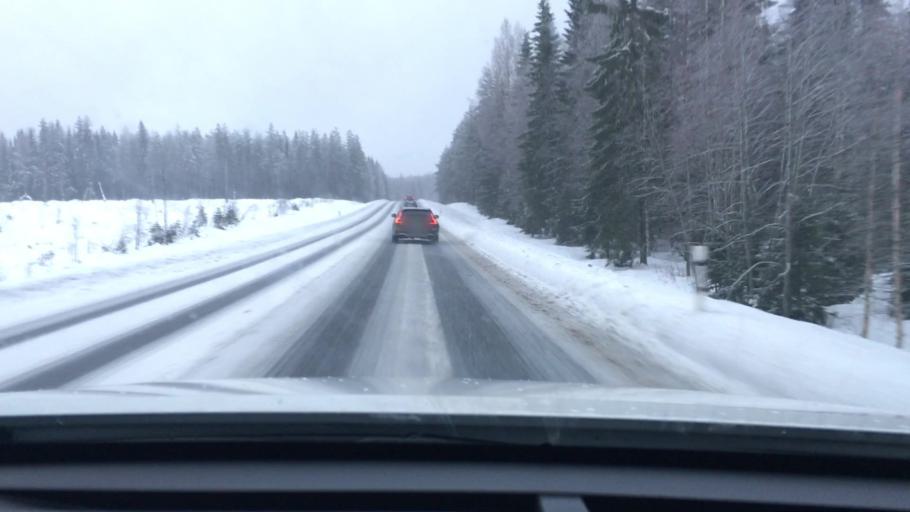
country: FI
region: Northern Savo
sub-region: Ylae-Savo
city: Sonkajaervi
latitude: 63.7736
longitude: 27.4153
